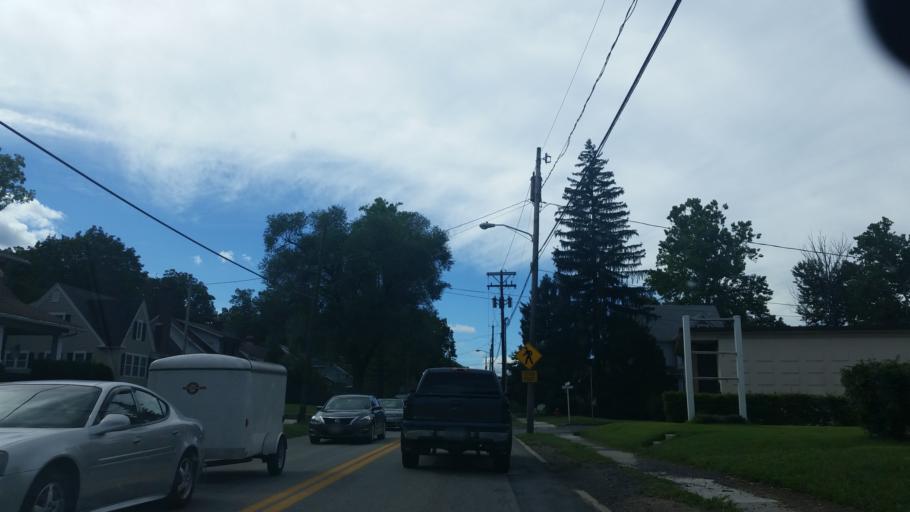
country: US
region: West Virginia
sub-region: Morgan County
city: Berkeley Springs
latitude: 39.6233
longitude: -78.2299
